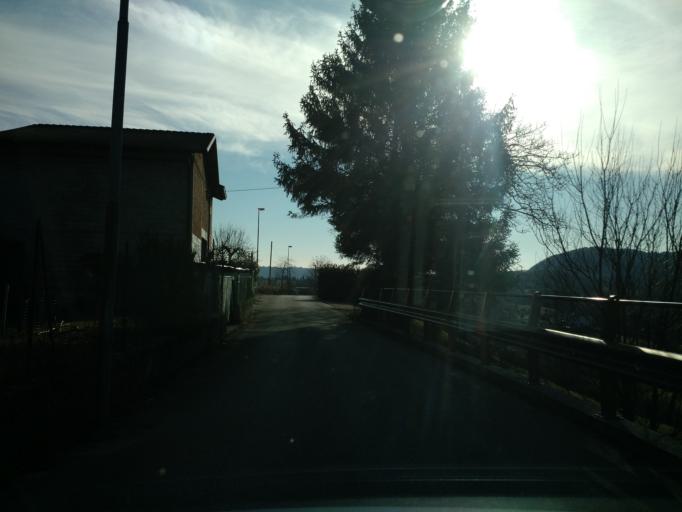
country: IT
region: Veneto
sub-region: Provincia di Vicenza
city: Cogollo del Cengio
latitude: 45.7941
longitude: 11.4015
